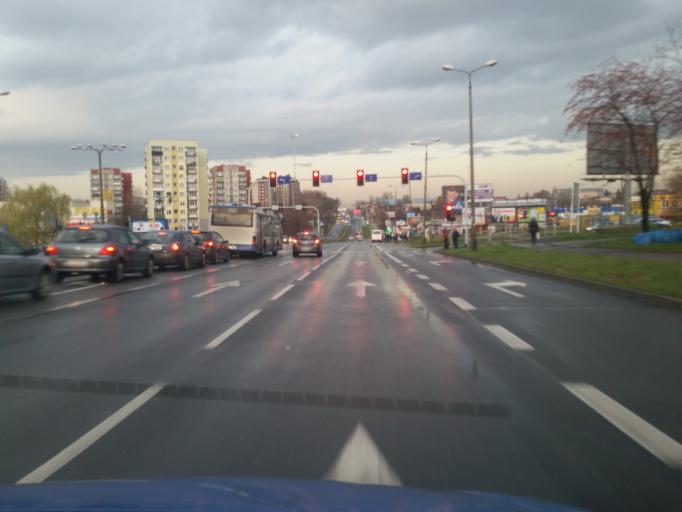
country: PL
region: Silesian Voivodeship
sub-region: Dabrowa Gornicza
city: Dabrowa Gornicza
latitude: 50.2896
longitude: 19.1805
